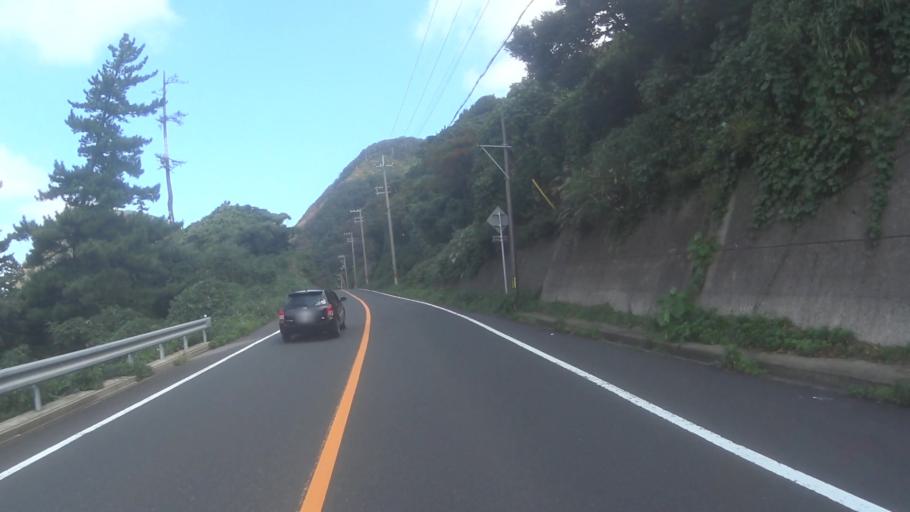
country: JP
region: Kyoto
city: Miyazu
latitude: 35.7487
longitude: 135.1311
